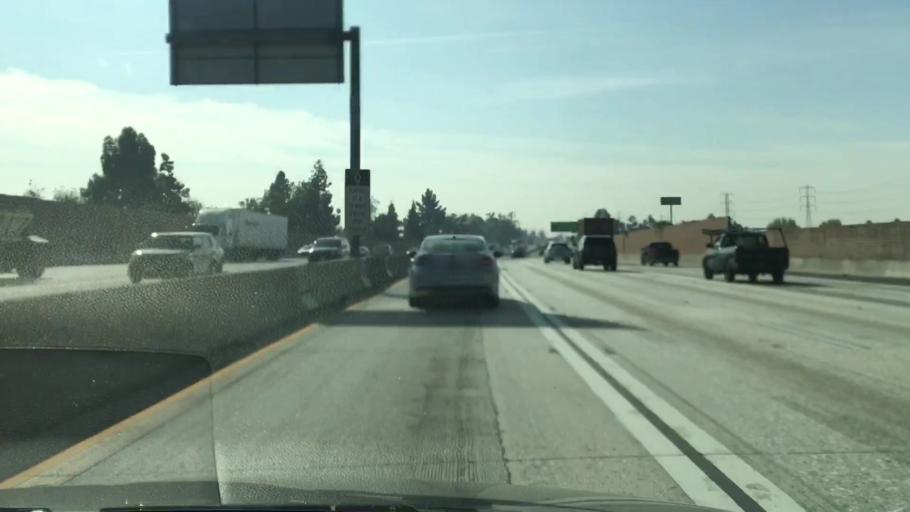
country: US
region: California
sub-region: Los Angeles County
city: West Whittier-Los Nietos
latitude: 33.9833
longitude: -118.0735
